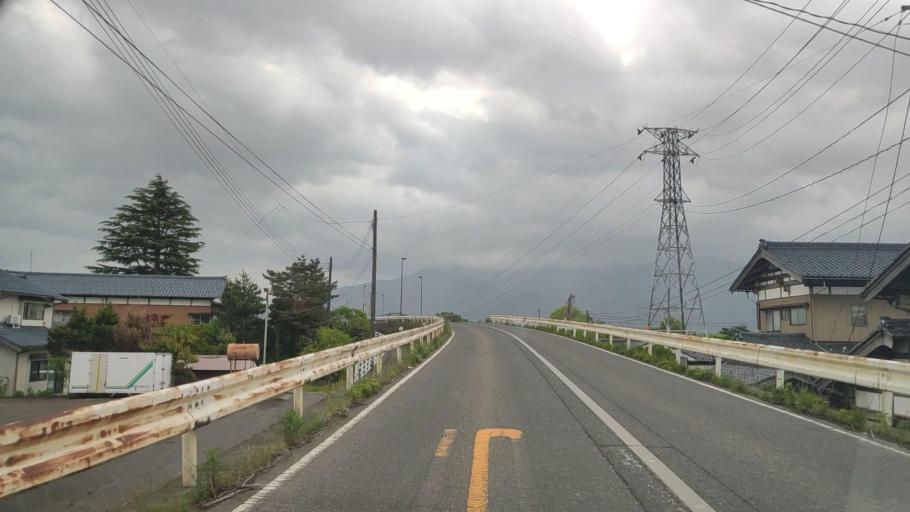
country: JP
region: Niigata
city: Gosen
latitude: 37.7329
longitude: 139.2003
